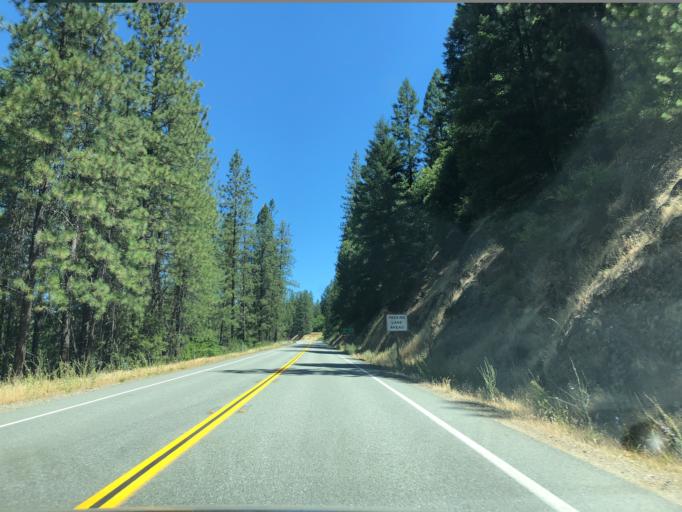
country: US
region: California
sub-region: Trinity County
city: Weaverville
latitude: 40.6552
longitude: -122.8963
